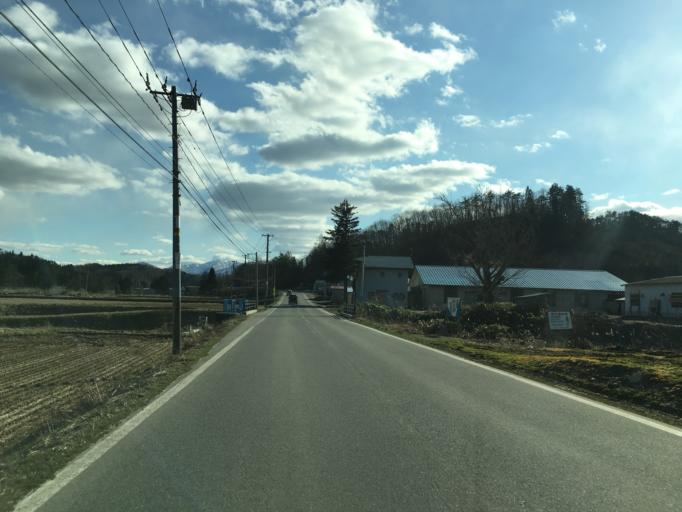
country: JP
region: Yamagata
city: Nagai
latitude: 37.9896
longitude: 140.0043
